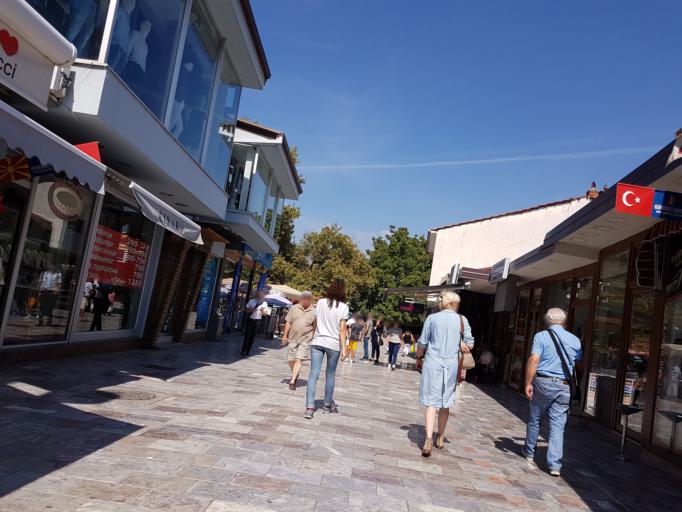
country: MK
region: Ohrid
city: Ohrid
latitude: 41.1155
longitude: 20.8004
